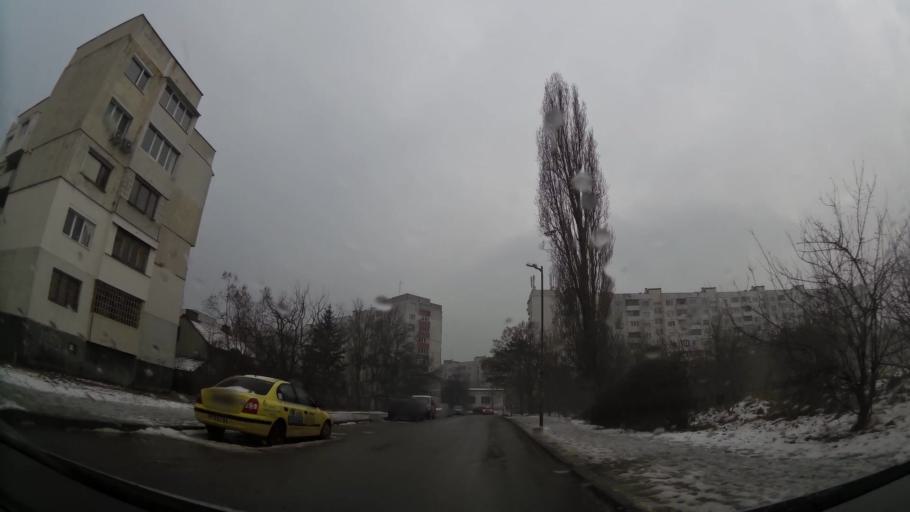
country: BG
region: Sofia-Capital
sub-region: Stolichna Obshtina
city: Sofia
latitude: 42.6852
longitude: 23.2638
